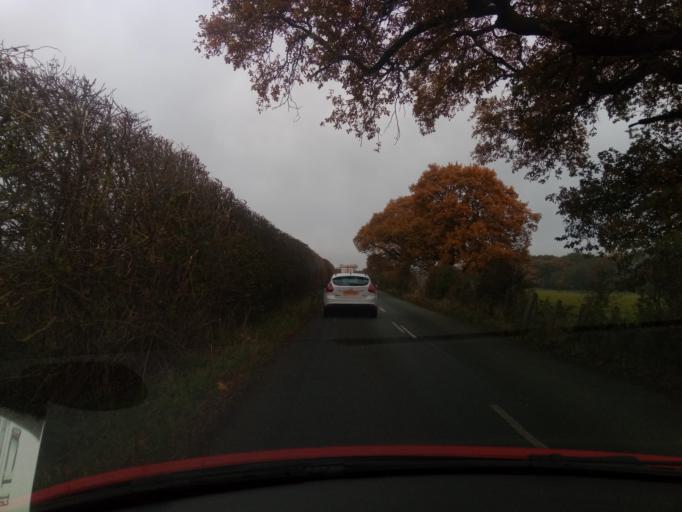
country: GB
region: England
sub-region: Derbyshire
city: Borrowash
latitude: 52.9392
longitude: -1.4063
